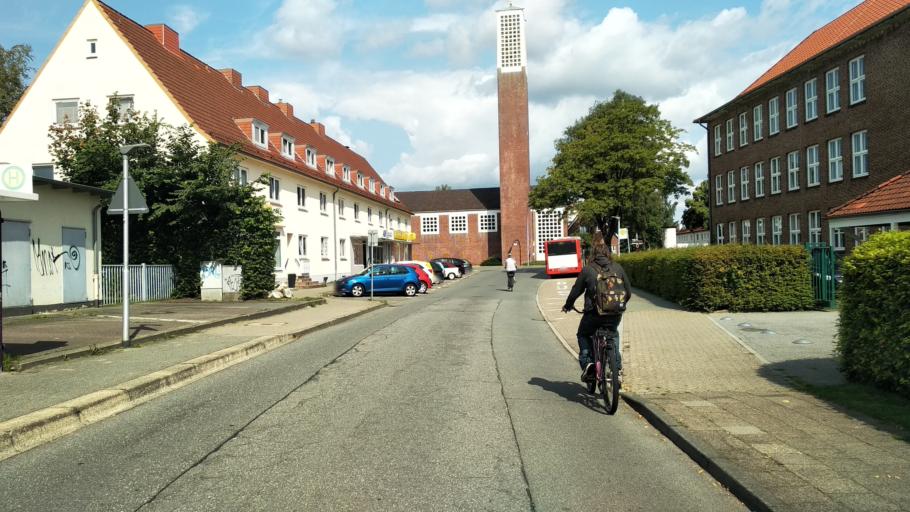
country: DE
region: Schleswig-Holstein
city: Schleswig
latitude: 54.5250
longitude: 9.5564
